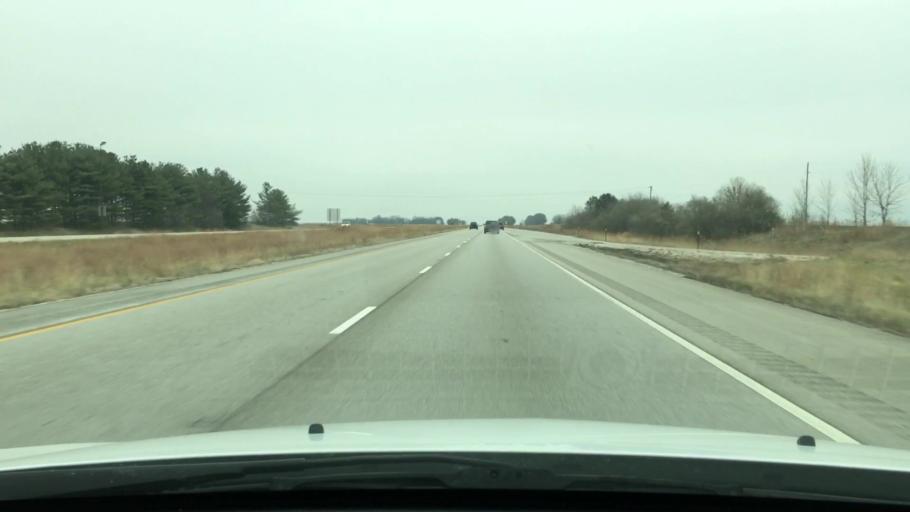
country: US
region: Illinois
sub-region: Sangamon County
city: New Berlin
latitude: 39.7368
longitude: -90.0383
